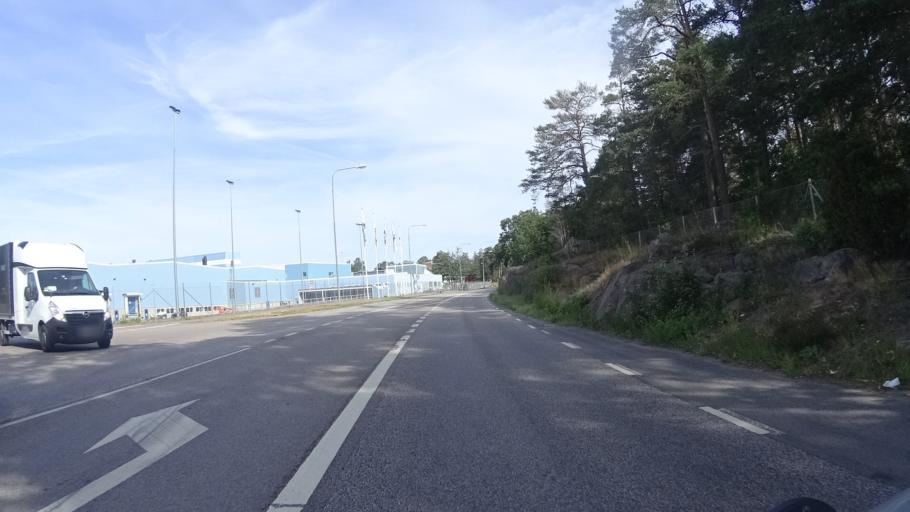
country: SE
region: Kalmar
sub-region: Oskarshamns Kommun
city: Oskarshamn
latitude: 57.2570
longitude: 16.4343
